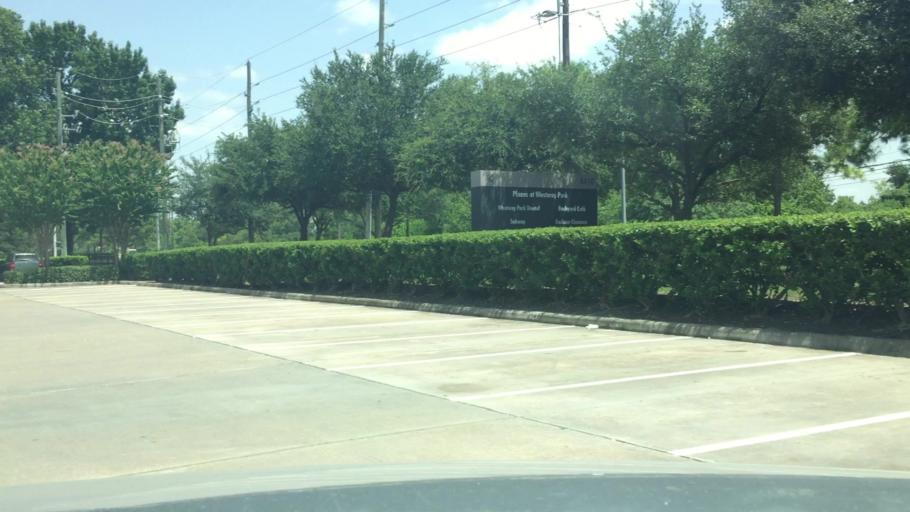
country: US
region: Texas
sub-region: Harris County
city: Jersey Village
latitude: 29.8324
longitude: -95.5593
